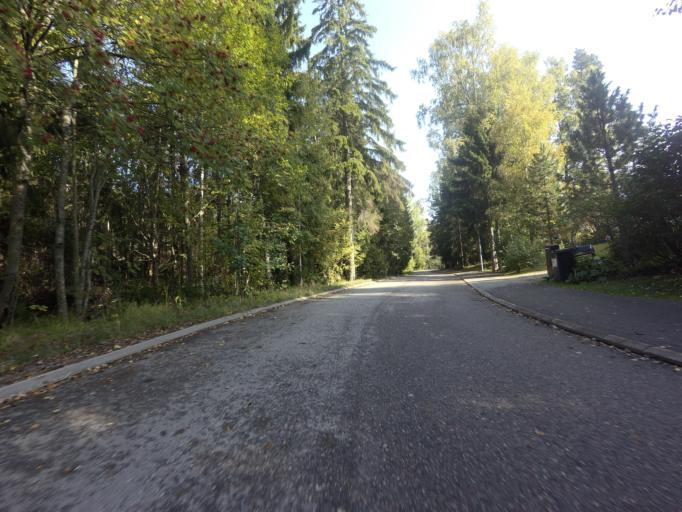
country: FI
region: Uusimaa
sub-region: Helsinki
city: Espoo
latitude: 60.1819
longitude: 24.6828
